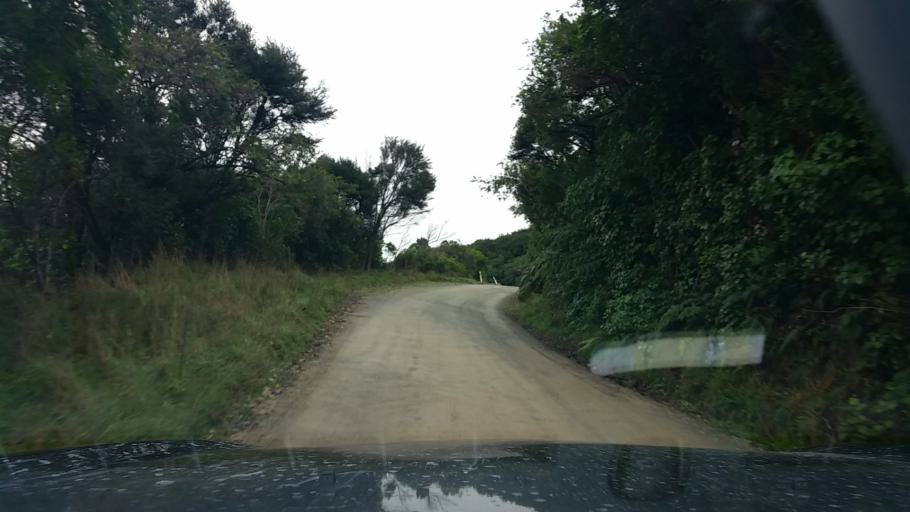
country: NZ
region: Marlborough
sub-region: Marlborough District
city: Picton
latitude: -41.1751
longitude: 174.0492
